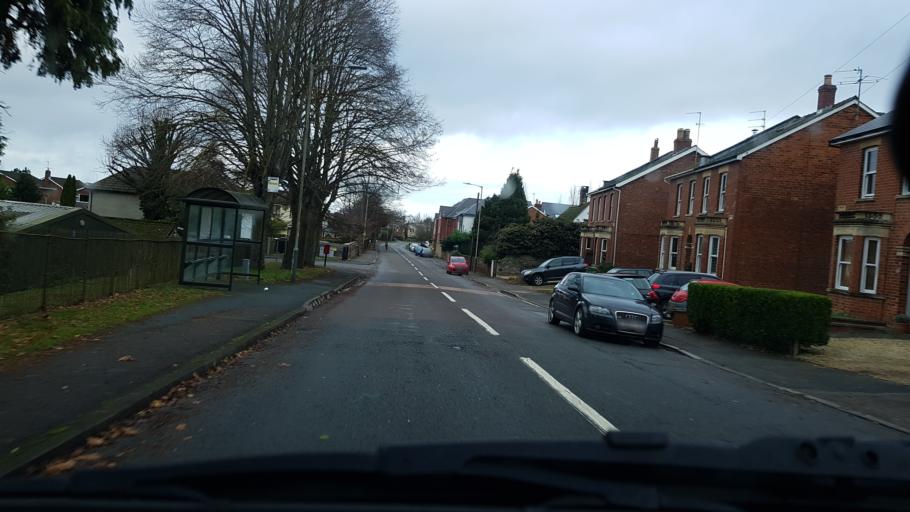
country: GB
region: England
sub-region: Gloucestershire
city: Charlton Kings
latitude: 51.8758
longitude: -2.0527
